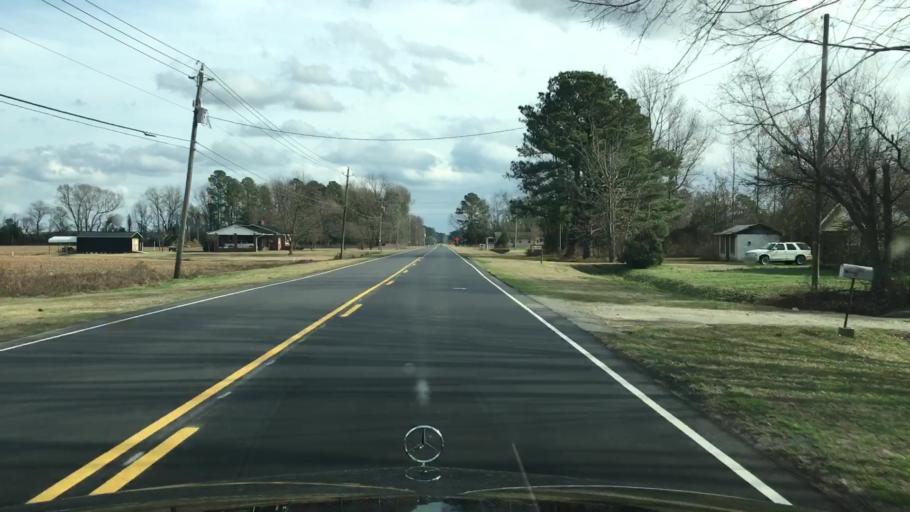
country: US
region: North Carolina
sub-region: Duplin County
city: Warsaw
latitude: 34.9821
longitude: -78.0356
